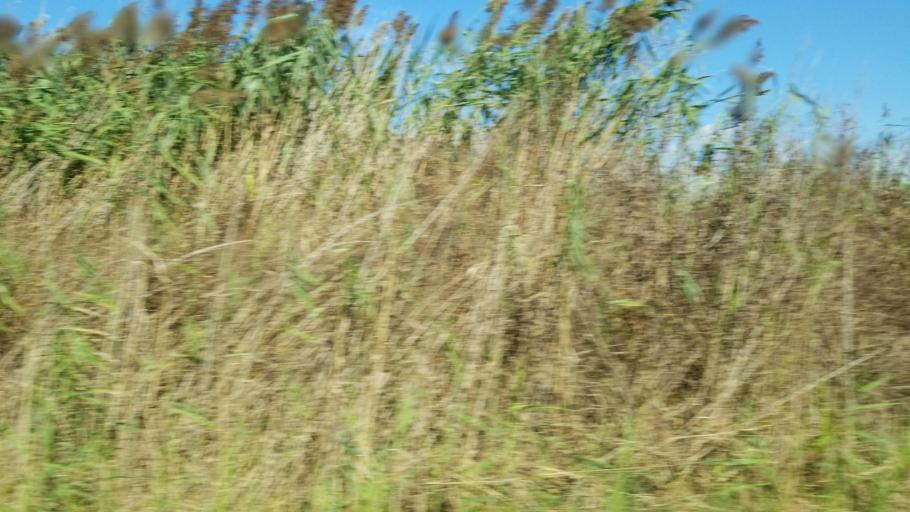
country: US
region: Illinois
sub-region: Saline County
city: Harrisburg
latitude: 37.8291
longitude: -88.5720
